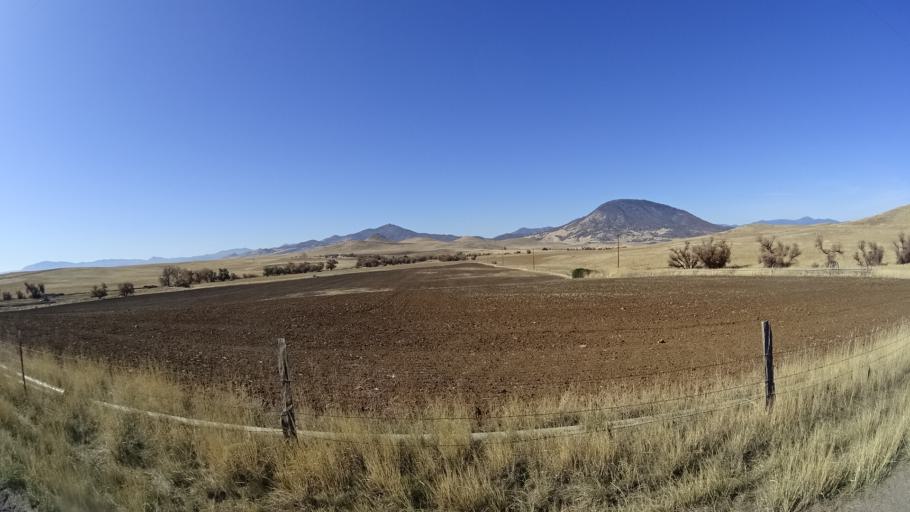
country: US
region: California
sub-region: Siskiyou County
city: Montague
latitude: 41.8258
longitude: -122.4205
